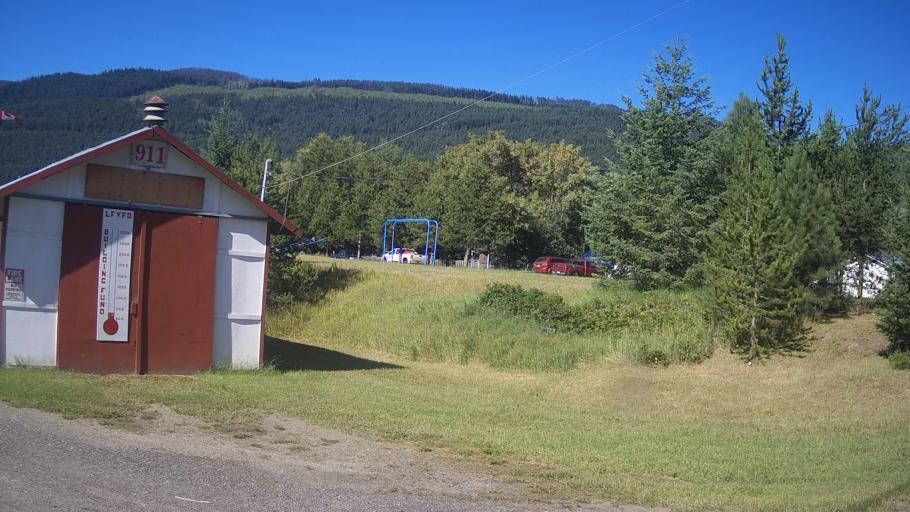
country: CA
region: British Columbia
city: Kamloops
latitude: 51.4247
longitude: -120.2071
